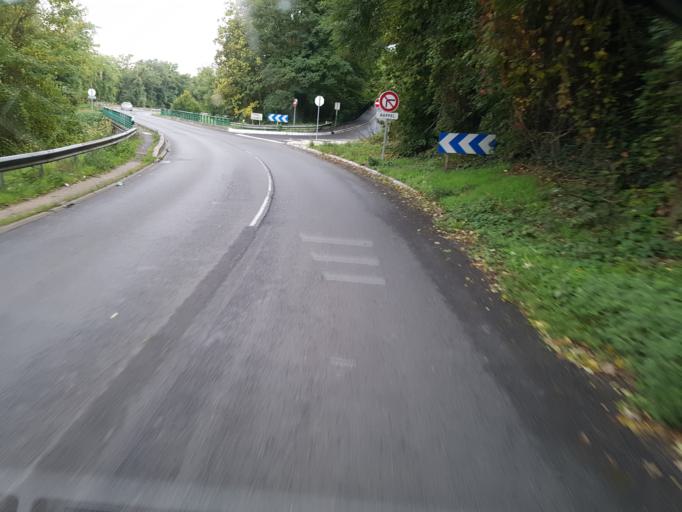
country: FR
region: Ile-de-France
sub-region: Departement de Seine-et-Marne
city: Meaux
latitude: 48.9645
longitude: 2.8699
